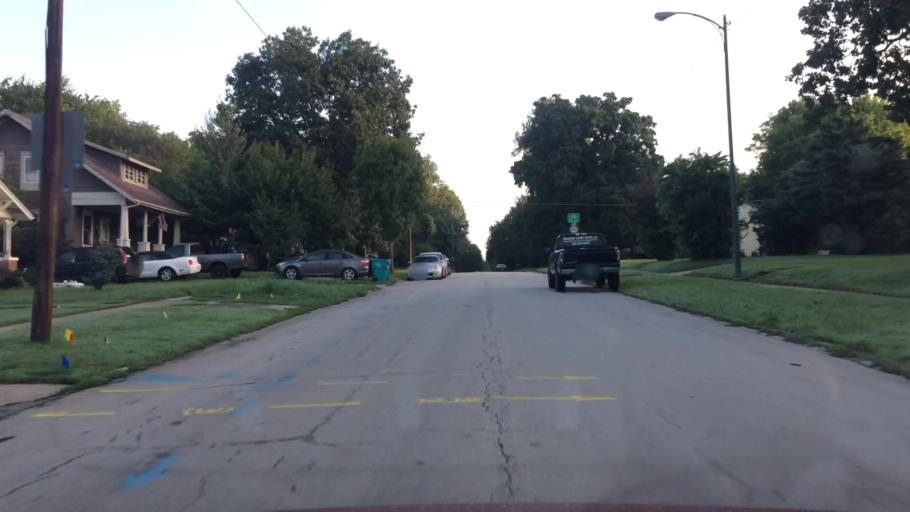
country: US
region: Missouri
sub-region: Greene County
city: Springfield
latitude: 37.2206
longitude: -93.2810
